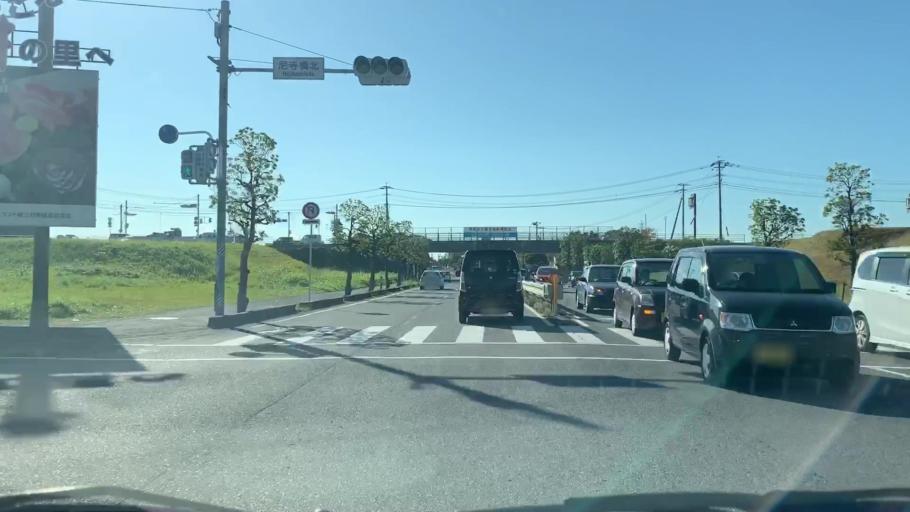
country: JP
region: Saga Prefecture
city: Saga-shi
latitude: 33.3103
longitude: 130.2764
